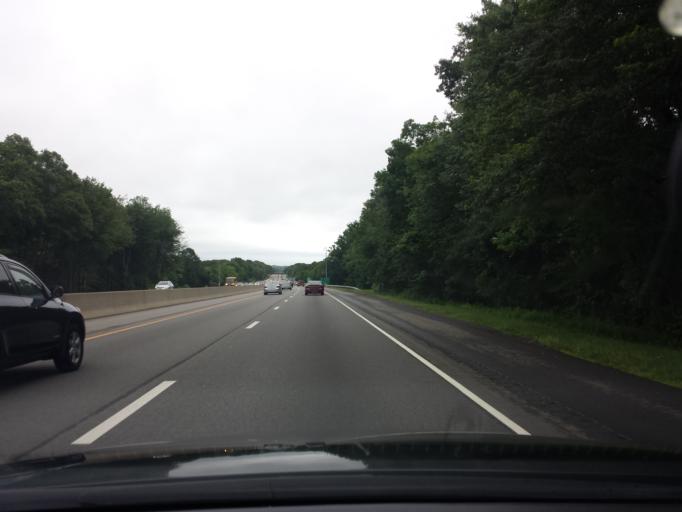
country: US
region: Connecticut
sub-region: New Haven County
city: Guilford Center
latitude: 41.2888
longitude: -72.6520
